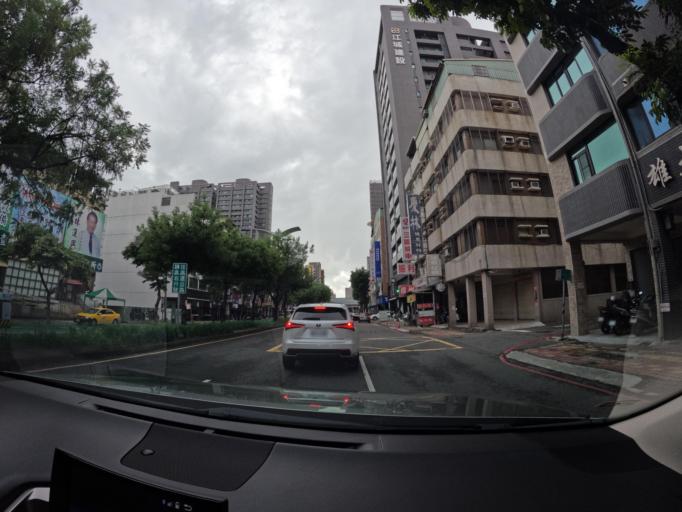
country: TW
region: Taiwan
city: Fengshan
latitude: 22.6371
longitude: 120.3396
